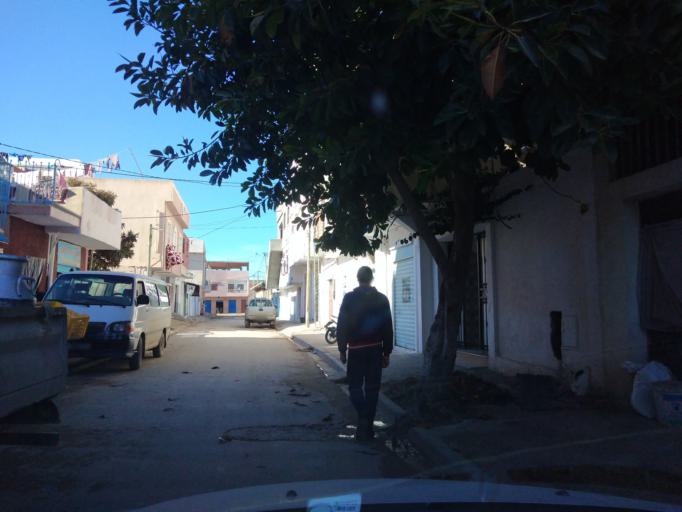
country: TN
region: Ariana
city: Qal'at al Andalus
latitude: 37.0658
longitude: 10.1220
